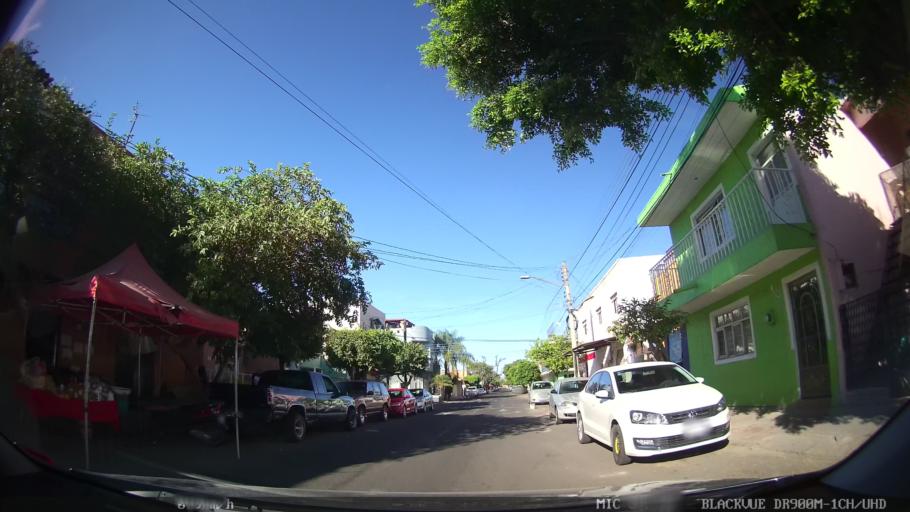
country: MX
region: Jalisco
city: Tlaquepaque
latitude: 20.7111
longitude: -103.2968
